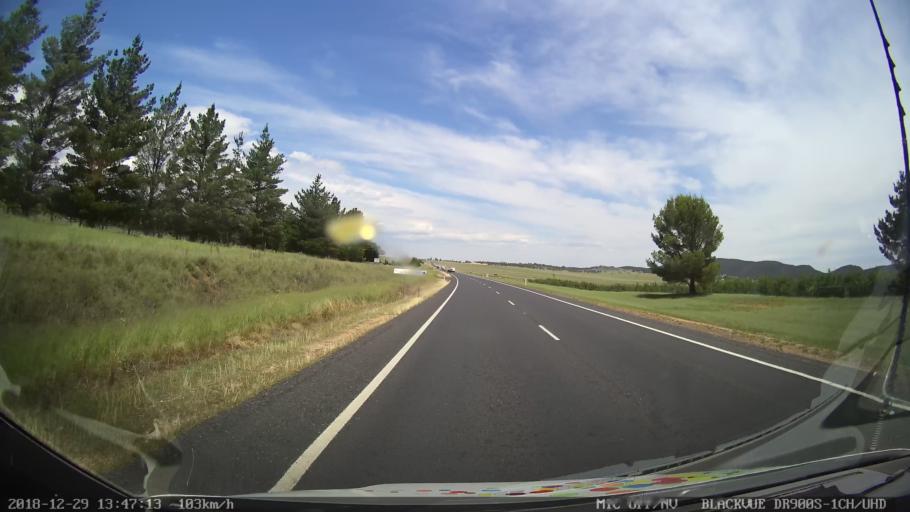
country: AU
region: New South Wales
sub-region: Cooma-Monaro
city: Cooma
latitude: -36.1224
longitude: 149.1416
